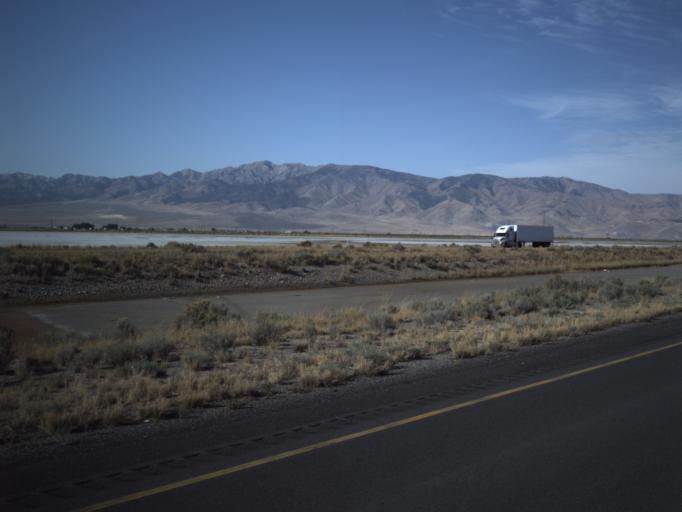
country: US
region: Utah
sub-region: Tooele County
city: Grantsville
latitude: 40.6797
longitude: -112.4157
